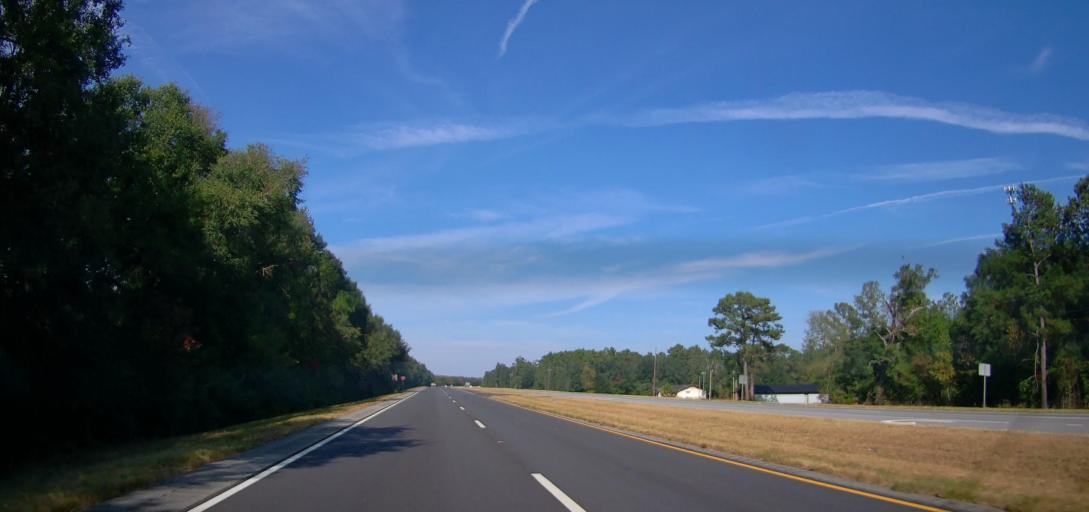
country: US
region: Georgia
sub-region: Dougherty County
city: Putney
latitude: 31.3938
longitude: -84.1467
